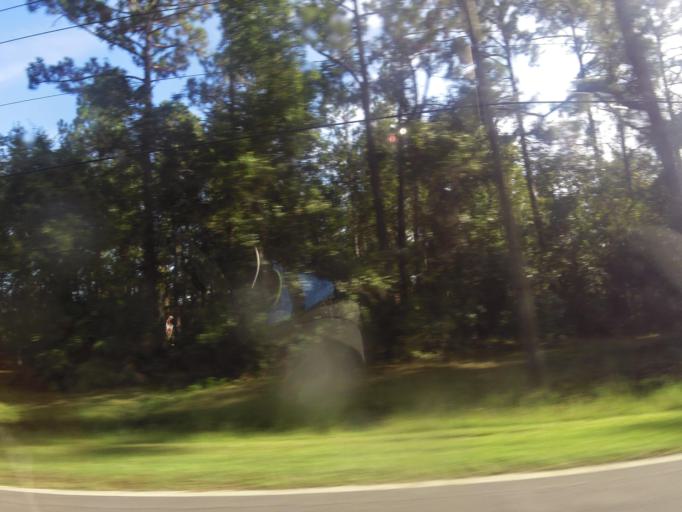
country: US
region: Florida
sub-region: Clay County
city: Green Cove Springs
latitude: 29.9161
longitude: -81.5851
